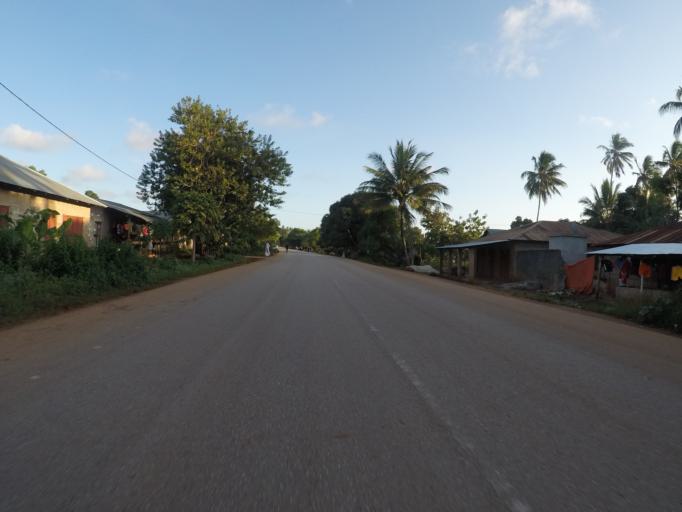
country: TZ
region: Zanzibar North
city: Mkokotoni
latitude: -5.8593
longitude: 39.2806
